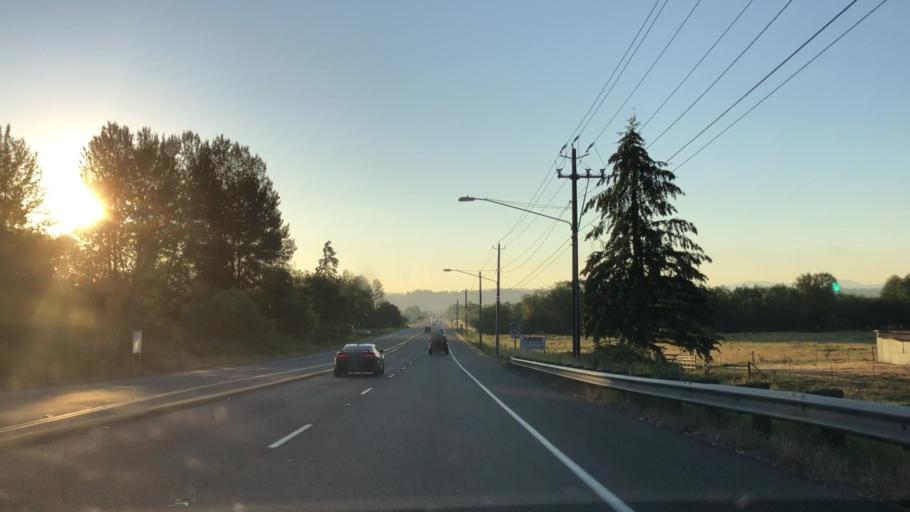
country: US
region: Washington
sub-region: King County
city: Lakeland North
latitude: 47.3535
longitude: -122.2635
